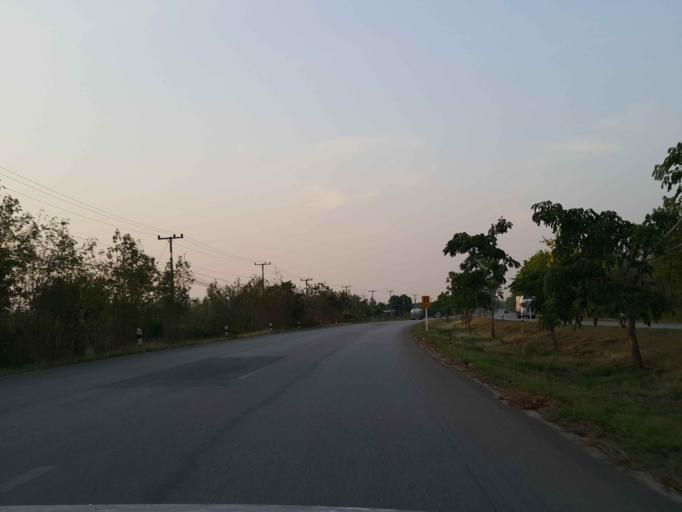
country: TH
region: Lampang
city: Sop Prap
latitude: 17.9982
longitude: 99.3551
